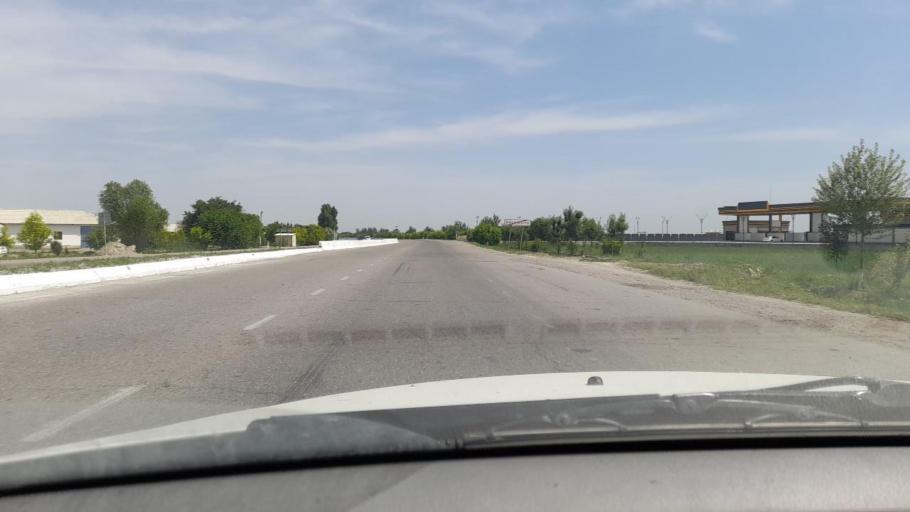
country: UZ
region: Bukhara
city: Galaosiyo
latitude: 39.8696
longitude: 64.4536
